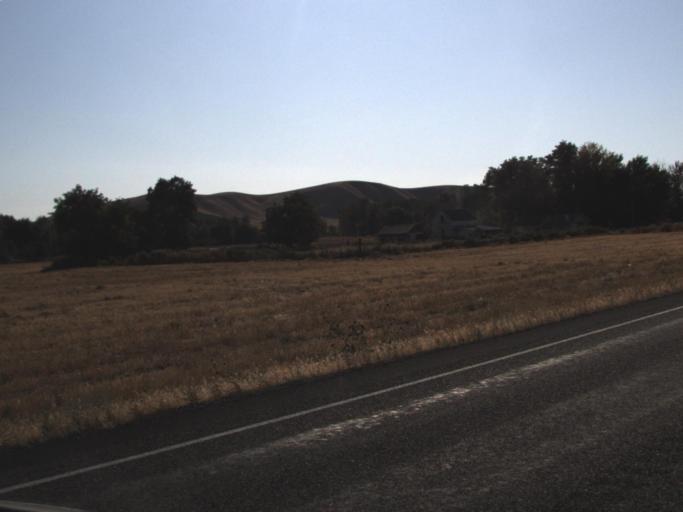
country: US
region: Washington
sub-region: Walla Walla County
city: Waitsburg
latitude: 46.2997
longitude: -118.3748
